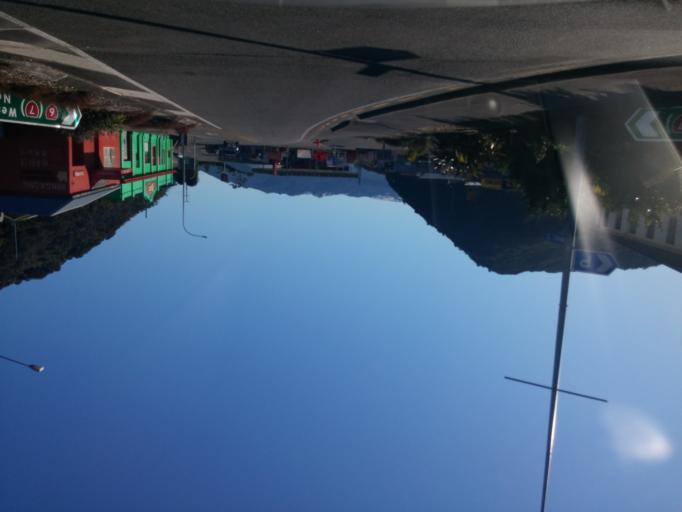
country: NZ
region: West Coast
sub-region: Grey District
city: Greymouth
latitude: -42.4500
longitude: 171.2112
